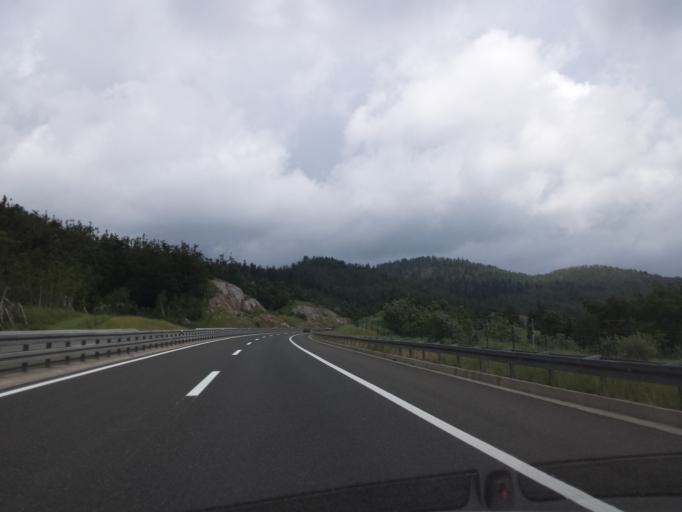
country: HR
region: Primorsko-Goranska
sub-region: Grad Delnice
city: Delnice
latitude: 45.3311
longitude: 14.7387
